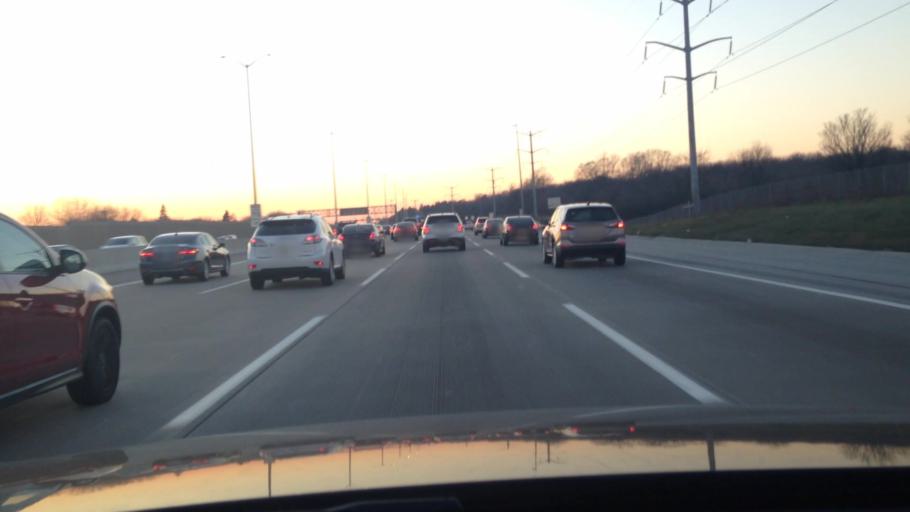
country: US
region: Illinois
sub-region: Cook County
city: Hoffman Estates
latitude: 42.0660
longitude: -88.0957
